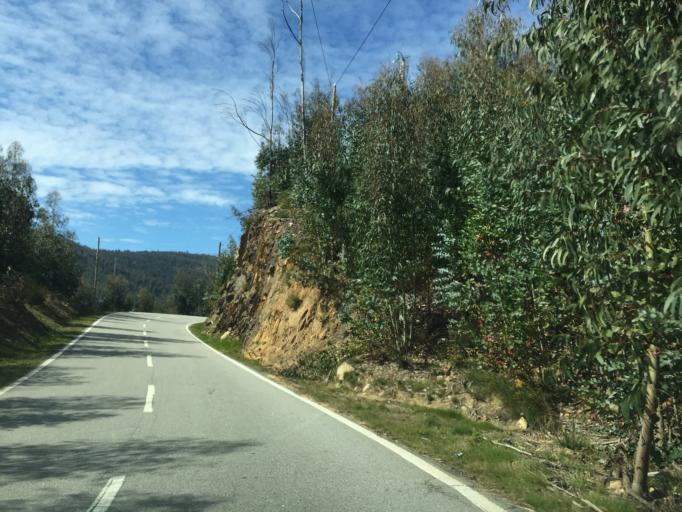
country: PT
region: Aveiro
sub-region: Arouca
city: Arouca
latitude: 40.9562
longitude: -8.1926
